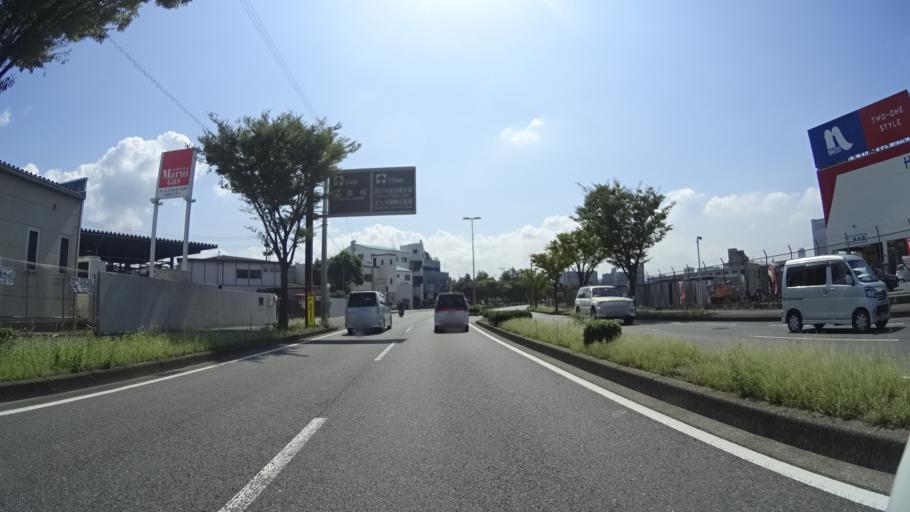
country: JP
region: Yamaguchi
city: Shimonoseki
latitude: 33.8883
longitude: 130.8955
